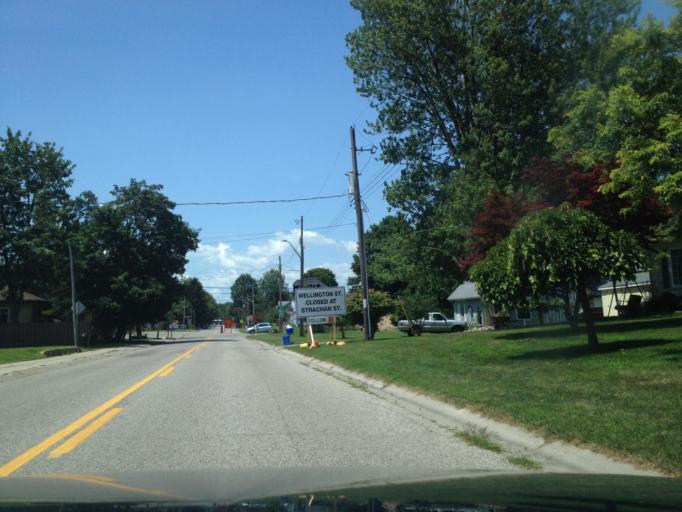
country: CA
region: Ontario
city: Aylmer
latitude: 42.6467
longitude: -80.7992
